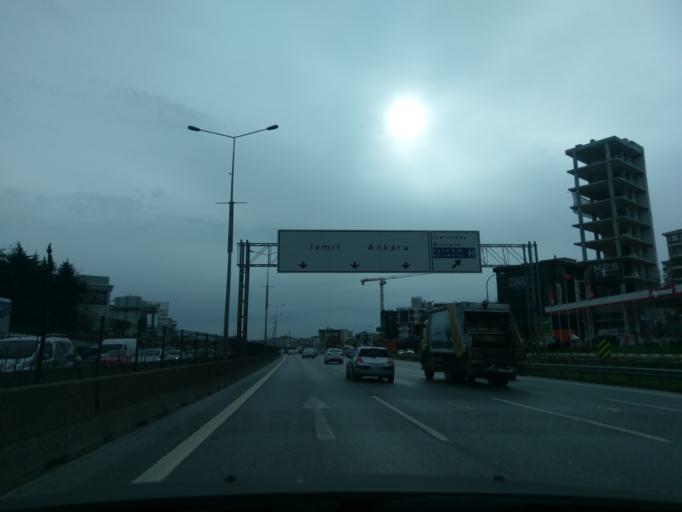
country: TR
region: Istanbul
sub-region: Atasehir
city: Atasehir
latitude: 40.9682
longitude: 29.1029
